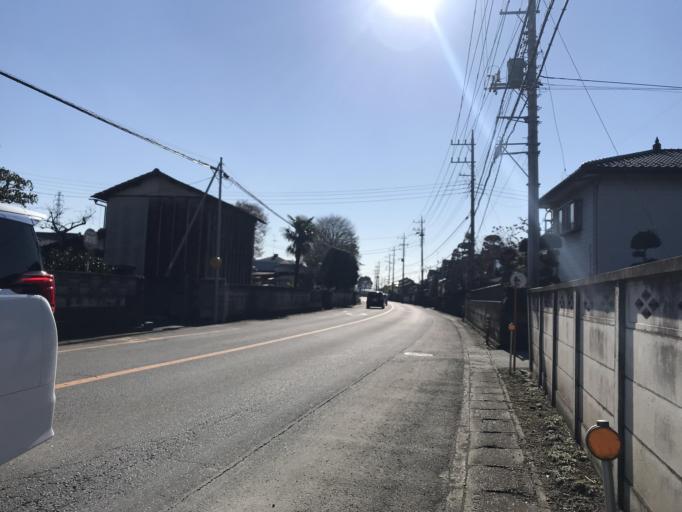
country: JP
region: Ibaraki
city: Sakai
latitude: 36.1507
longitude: 139.8118
